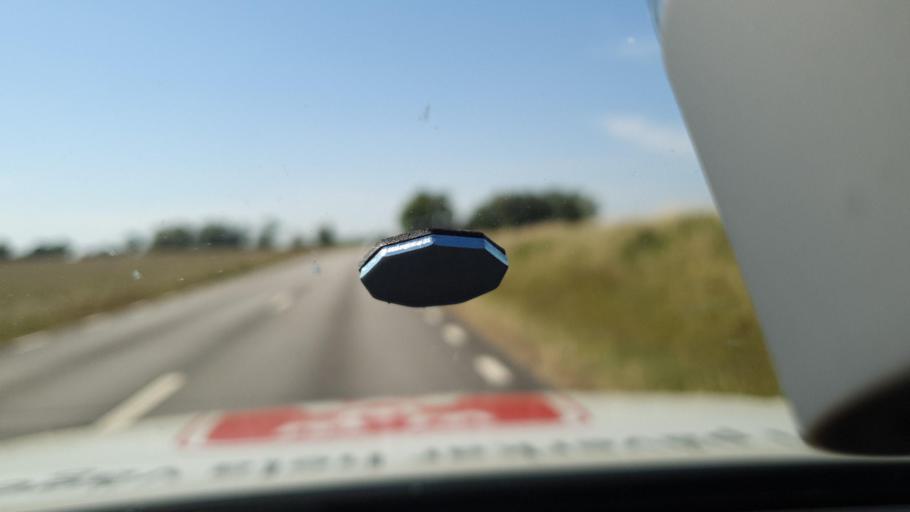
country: SE
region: Skane
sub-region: Svedala Kommun
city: Svedala
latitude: 55.4489
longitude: 13.2627
